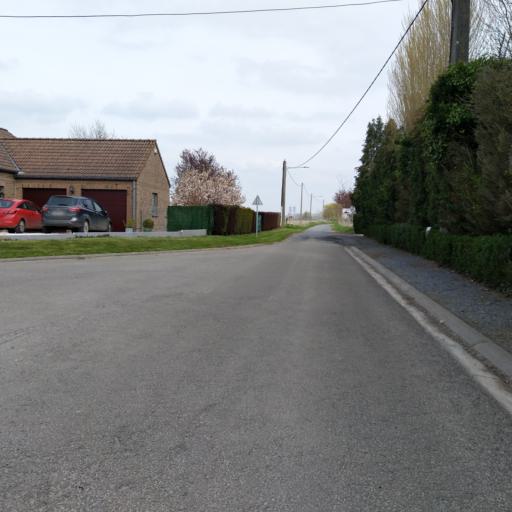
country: BE
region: Wallonia
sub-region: Province du Hainaut
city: Quevy-le-Petit
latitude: 50.3385
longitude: 3.9136
